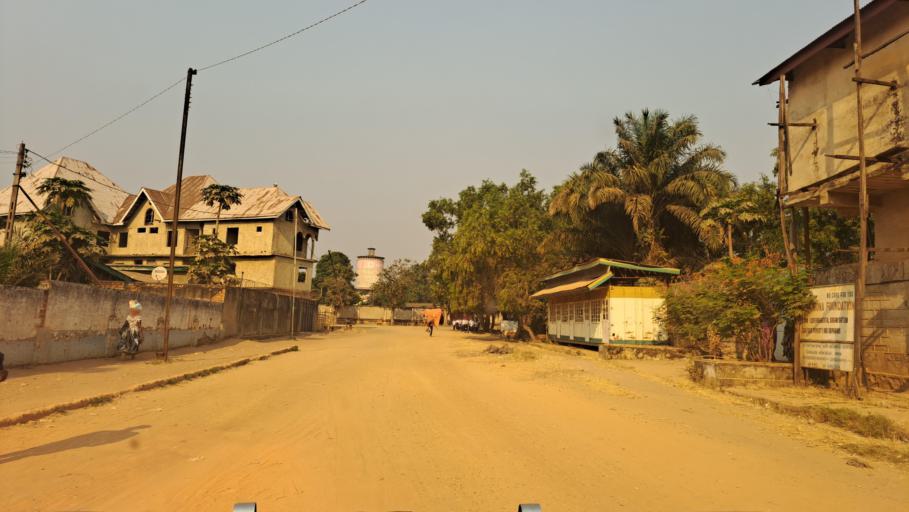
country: CD
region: Kasai-Occidental
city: Kananga
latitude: -5.8926
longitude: 22.4120
